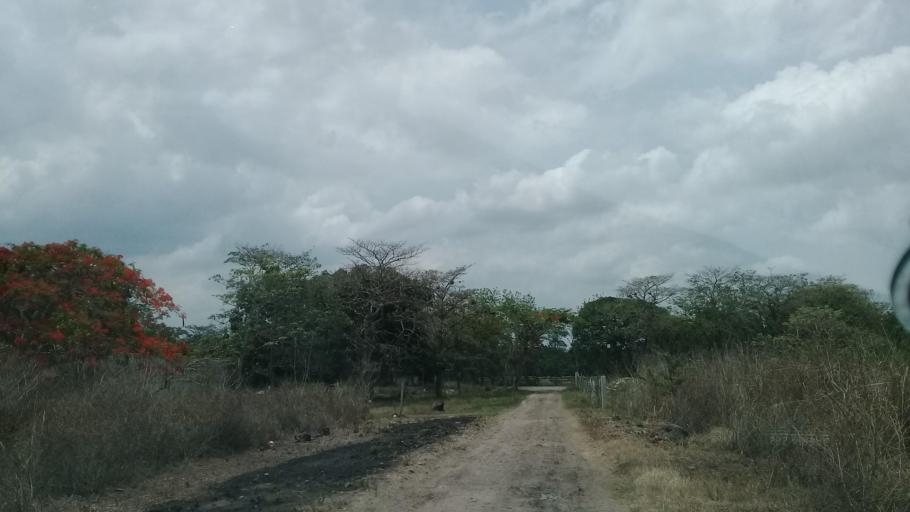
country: MX
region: Veracruz
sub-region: Emiliano Zapata
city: Plan del Rio
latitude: 19.4279
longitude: -96.6960
